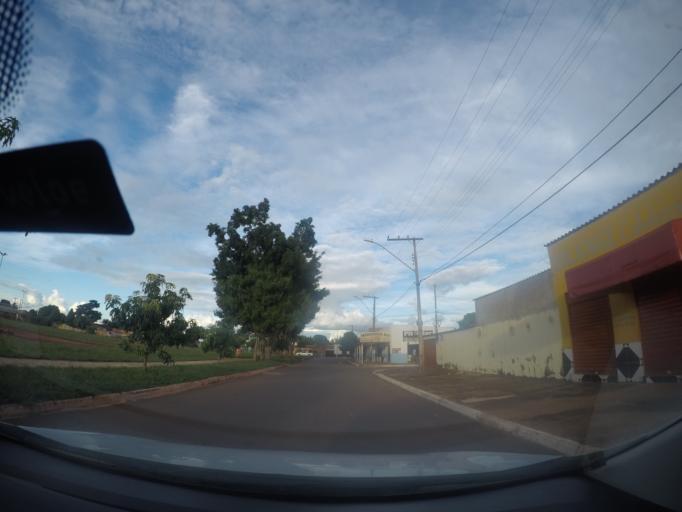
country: BR
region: Goias
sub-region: Goianira
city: Goianira
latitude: -16.5879
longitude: -49.3706
